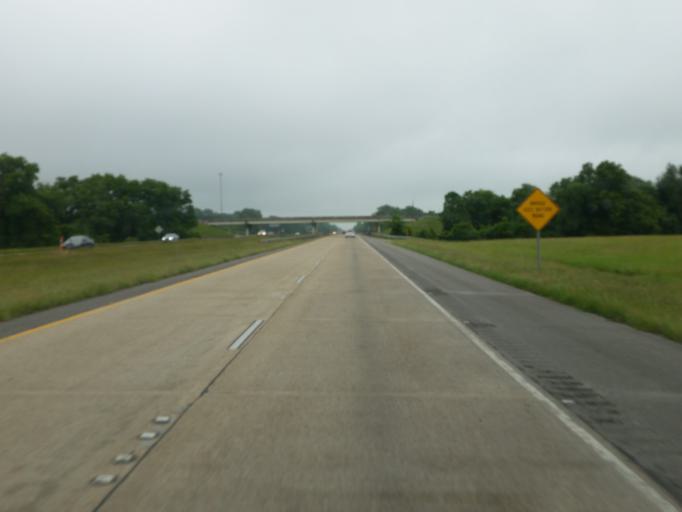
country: US
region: Louisiana
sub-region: Madison Parish
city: Tallulah
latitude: 32.3812
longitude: -91.1748
